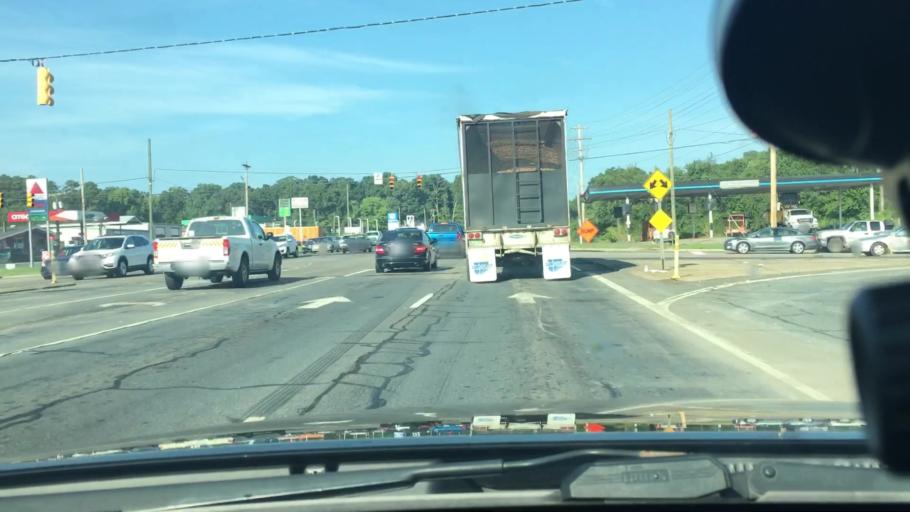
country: US
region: North Carolina
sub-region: Stanly County
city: Albemarle
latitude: 35.3384
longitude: -80.1990
